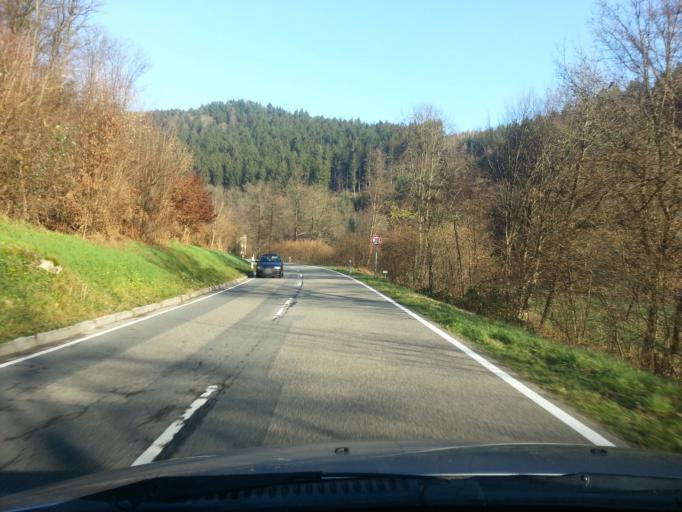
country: DE
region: Baden-Wuerttemberg
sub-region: Karlsruhe Region
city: Eberbach
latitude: 49.4926
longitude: 9.0444
